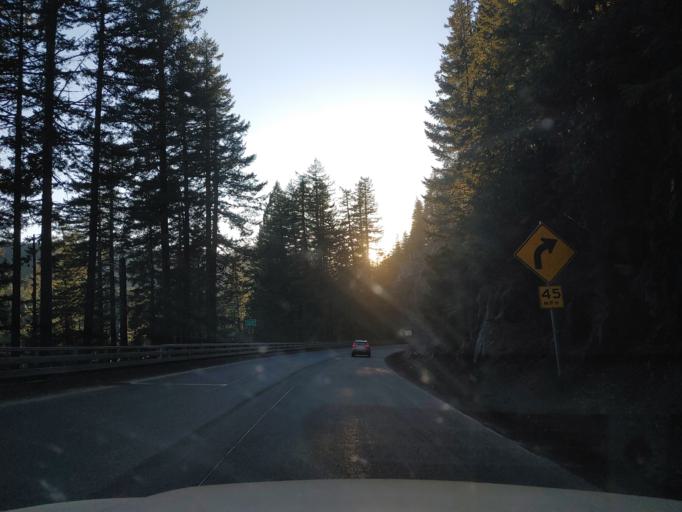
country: US
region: Oregon
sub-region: Lane County
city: Oakridge
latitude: 43.6138
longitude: -122.1309
